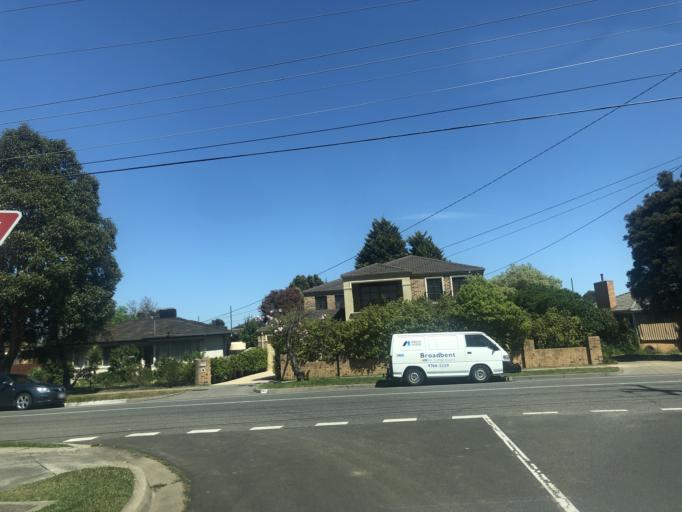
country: AU
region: Victoria
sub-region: Monash
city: Notting Hill
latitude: -37.8997
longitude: 145.1600
